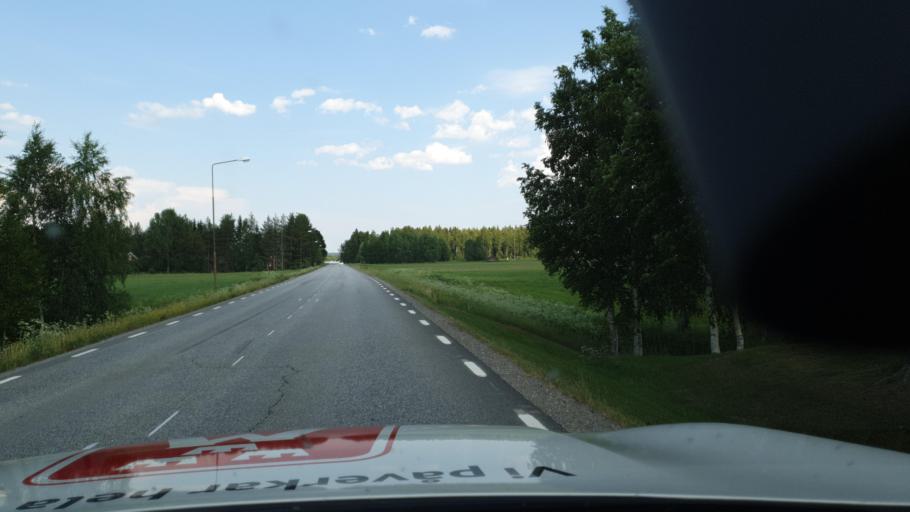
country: SE
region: Vaesterbotten
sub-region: Skelleftea Kommun
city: Viken
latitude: 64.7426
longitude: 20.8220
